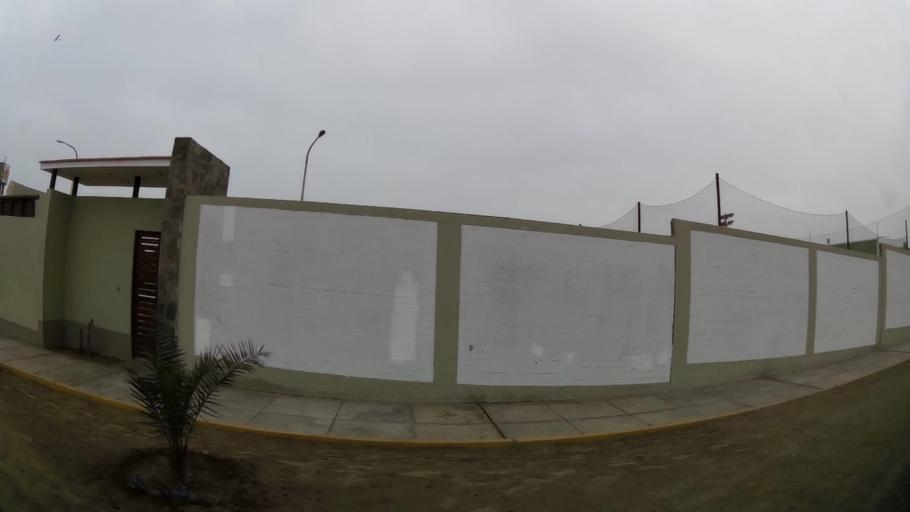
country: PE
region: Lima
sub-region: Lima
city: Punta Hermosa
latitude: -12.3253
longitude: -76.8276
